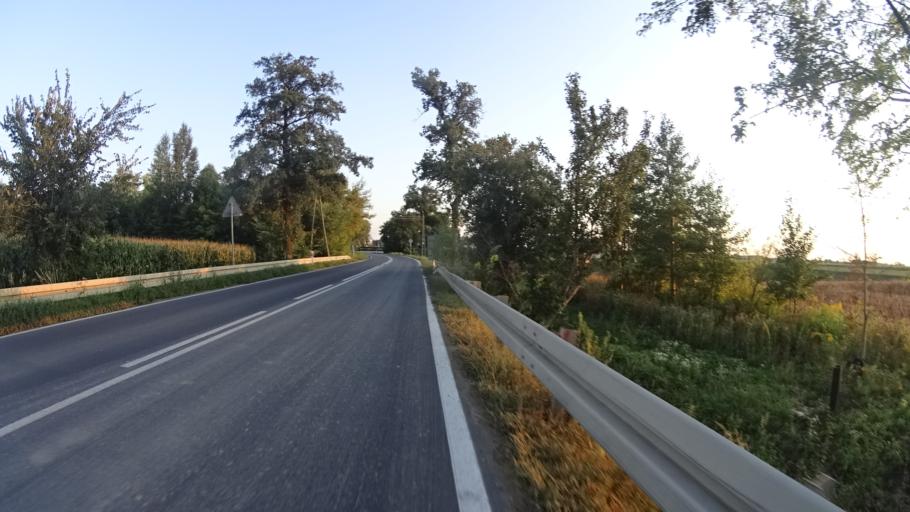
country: PL
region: Masovian Voivodeship
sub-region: Powiat warszawski zachodni
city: Ozarow Mazowiecki
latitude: 52.2195
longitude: 20.7731
